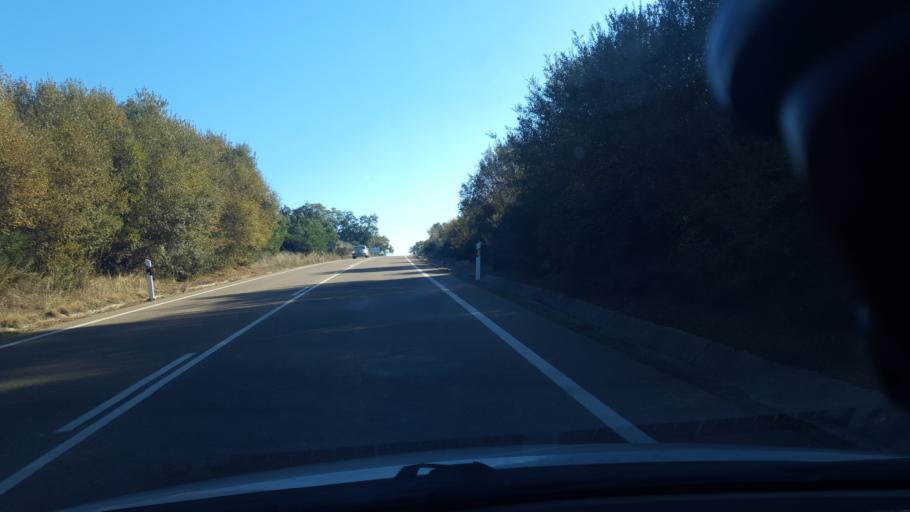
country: ES
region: Castille and Leon
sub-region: Provincia de Avila
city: Candeleda
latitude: 40.1365
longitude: -5.2376
